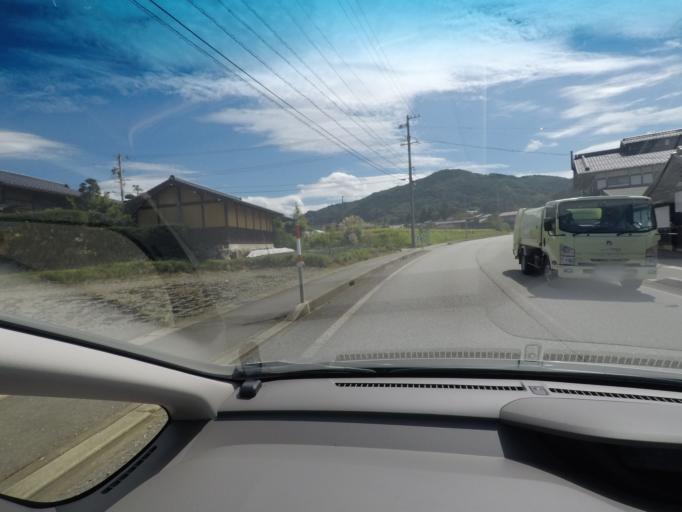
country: JP
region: Gifu
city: Takayama
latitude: 36.1355
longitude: 137.2919
